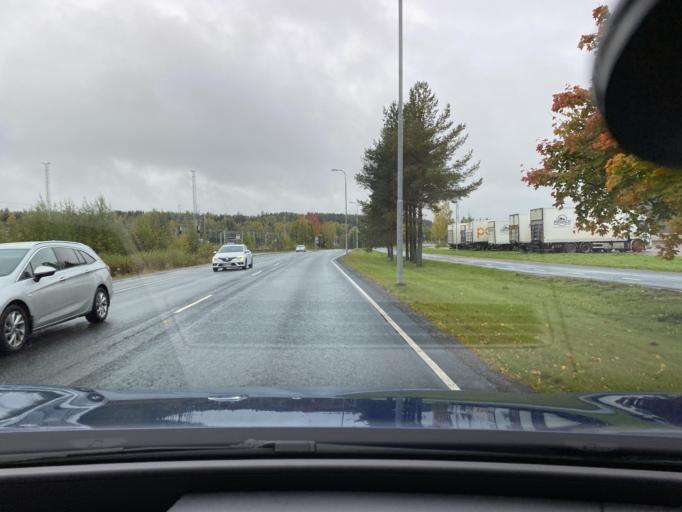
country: FI
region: Pirkanmaa
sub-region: Tampere
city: Tampere
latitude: 61.4677
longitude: 23.7611
